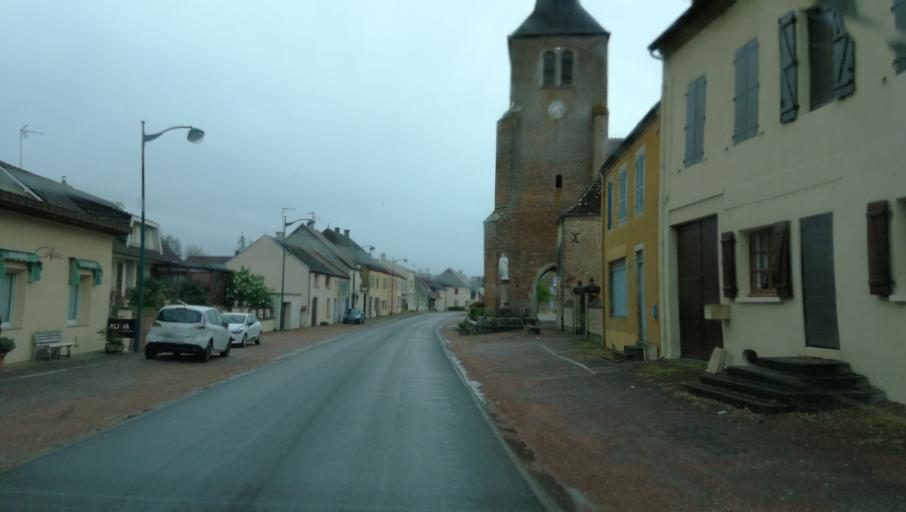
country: FR
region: Franche-Comte
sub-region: Departement du Jura
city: Petit-Noir
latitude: 46.8413
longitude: 5.3652
